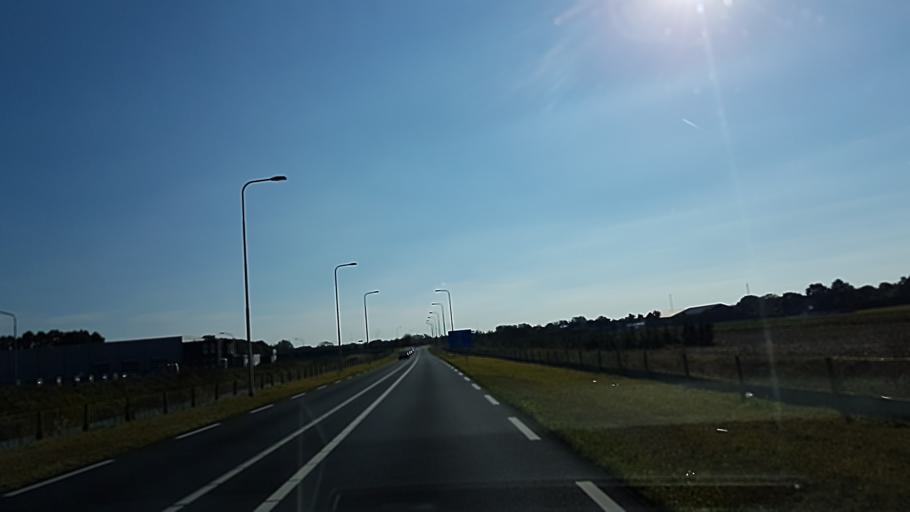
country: NL
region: North Brabant
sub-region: Gemeente Woensdrecht
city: Woensdrecht
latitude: 51.4269
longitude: 4.3409
